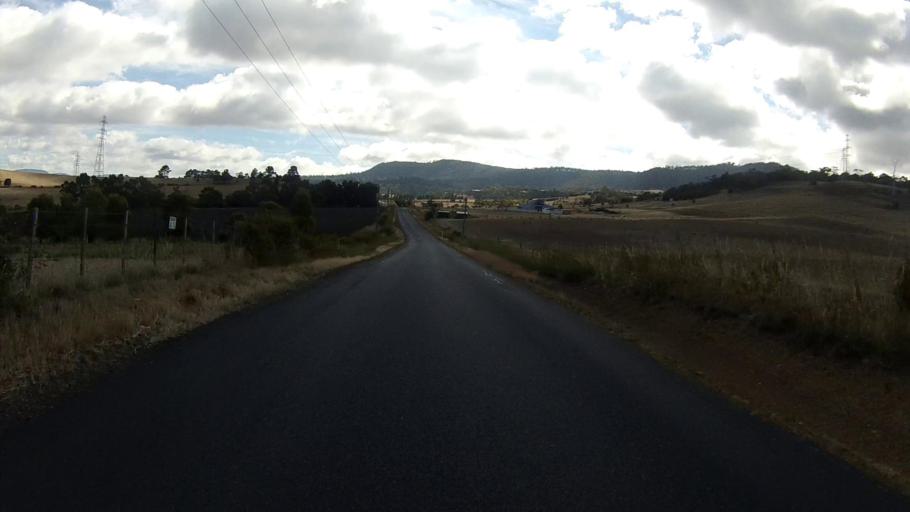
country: AU
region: Tasmania
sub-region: Brighton
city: Old Beach
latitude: -42.7708
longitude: 147.2927
